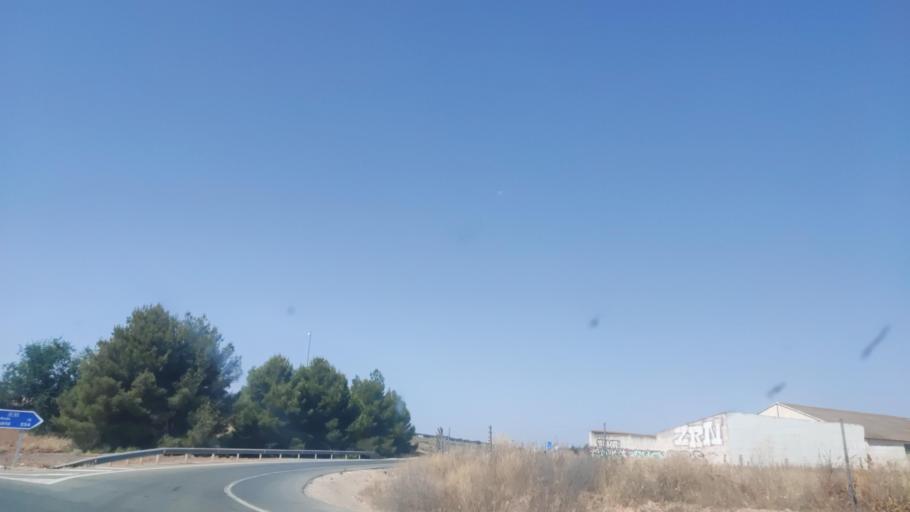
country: ES
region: Castille-La Mancha
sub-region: Provincia de Albacete
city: La Gineta
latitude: 39.1194
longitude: -1.9994
